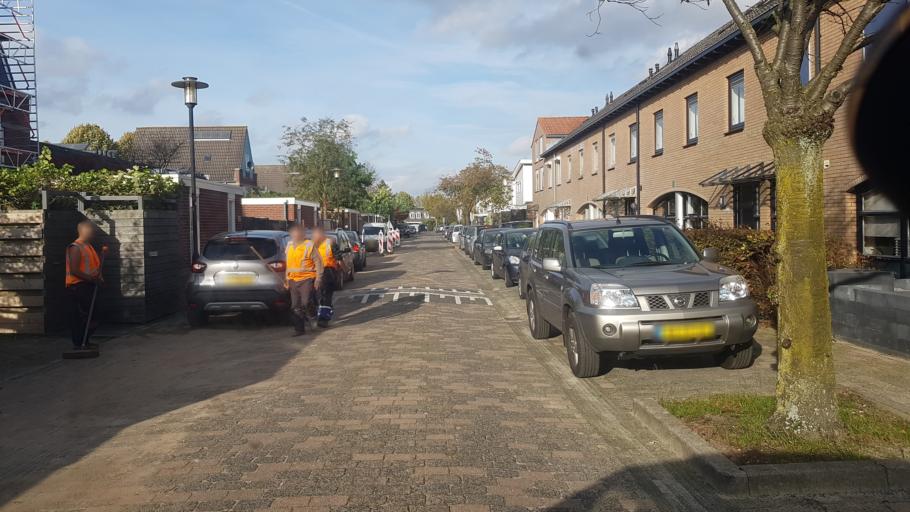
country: NL
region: Gelderland
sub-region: Gemeente Apeldoorn
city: Apeldoorn
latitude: 52.2126
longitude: 6.0088
